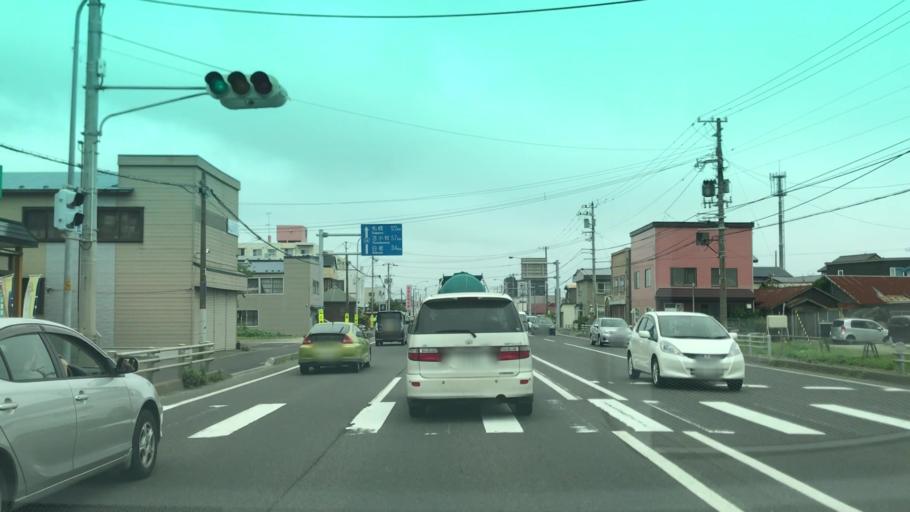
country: JP
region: Hokkaido
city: Muroran
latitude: 42.3567
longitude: 141.0501
